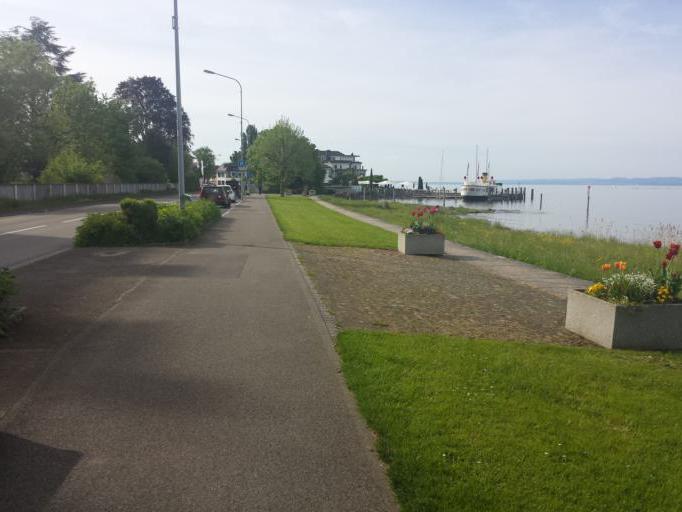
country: CH
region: Saint Gallen
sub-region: Wahlkreis Rorschach
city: Horn
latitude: 47.4930
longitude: 9.4701
